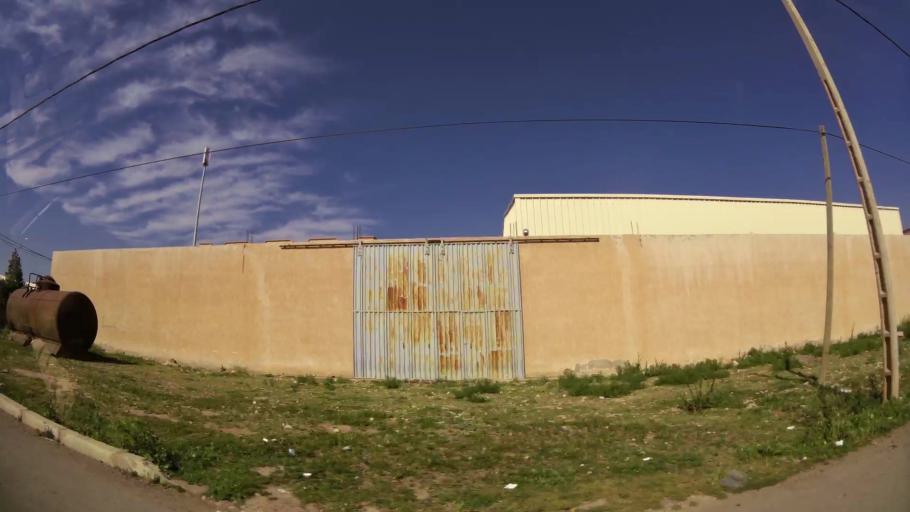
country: MA
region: Oriental
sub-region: Oujda-Angad
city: Oujda
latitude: 34.7015
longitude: -1.8848
